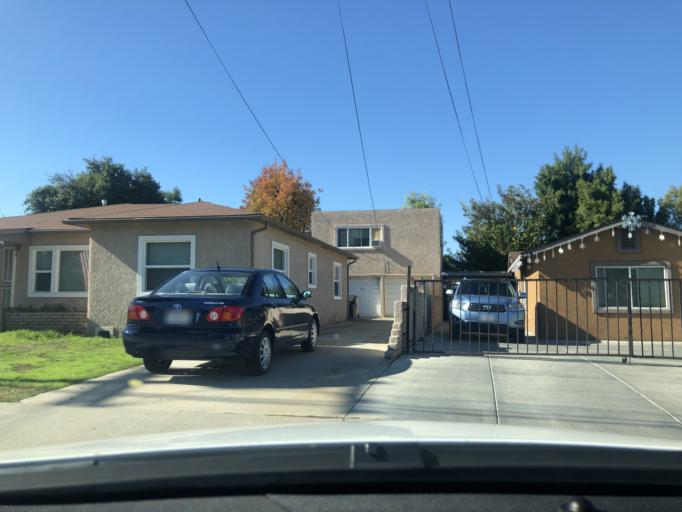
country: US
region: California
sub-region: San Diego County
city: El Cajon
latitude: 32.7853
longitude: -116.9483
